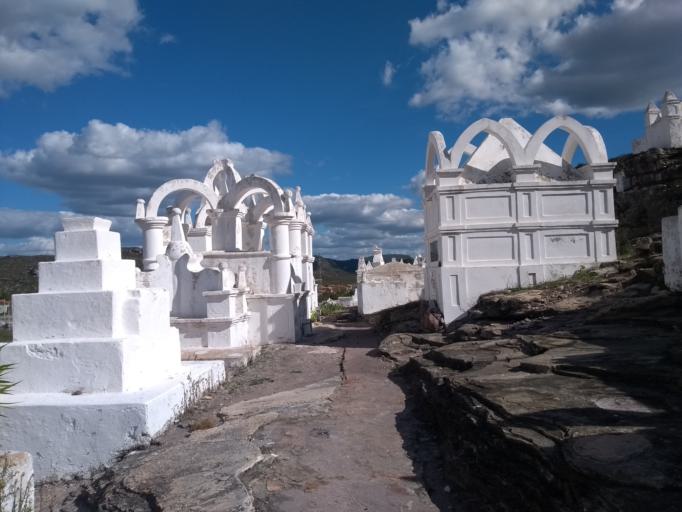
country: BR
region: Bahia
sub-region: Andarai
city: Vera Cruz
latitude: -13.0073
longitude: -41.3773
